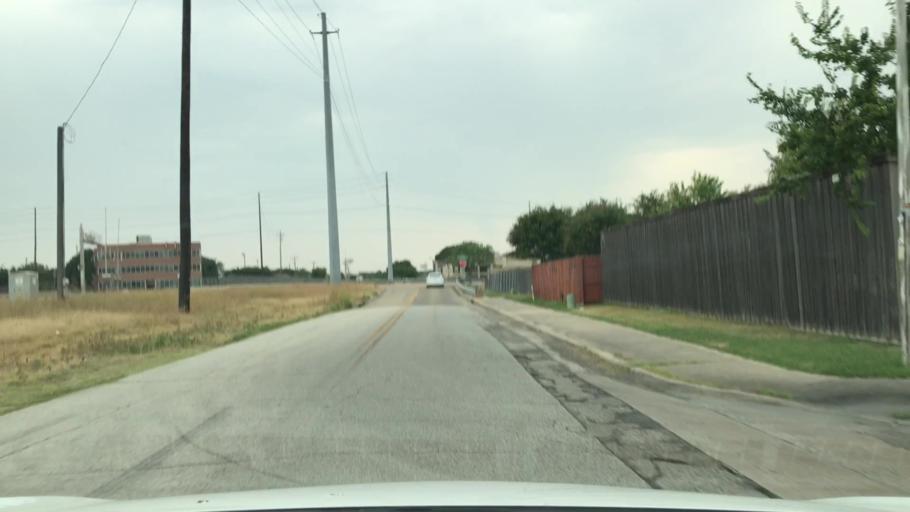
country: US
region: Texas
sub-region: Dallas County
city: Carrollton
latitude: 32.9872
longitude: -96.8758
